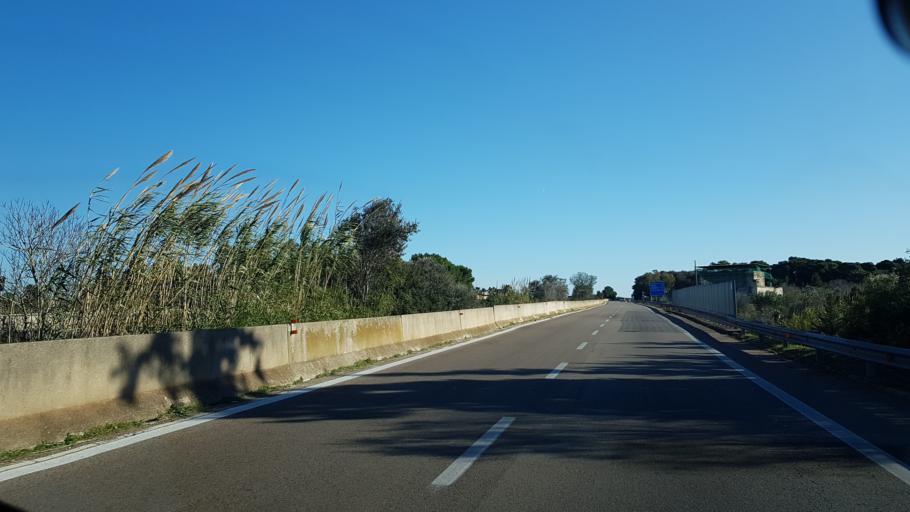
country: IT
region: Apulia
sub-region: Provincia di Lecce
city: Alezio
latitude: 40.0300
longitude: 18.0315
